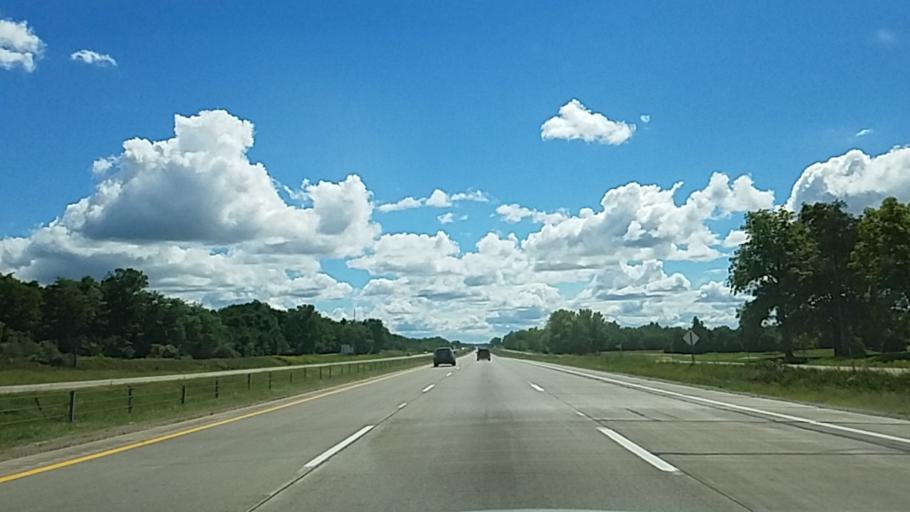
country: US
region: Michigan
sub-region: Genesee County
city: Linden
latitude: 42.7336
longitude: -83.7642
